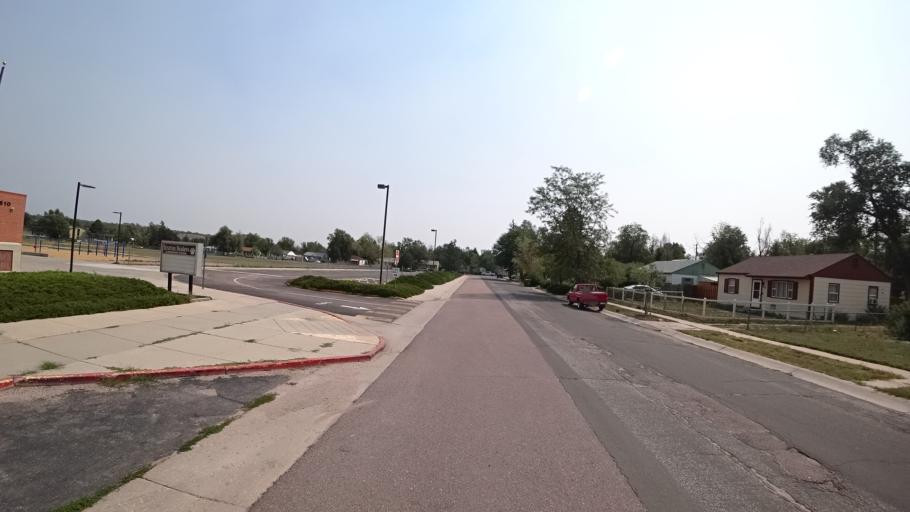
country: US
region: Colorado
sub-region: El Paso County
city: Colorado Springs
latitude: 38.8051
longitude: -104.8129
